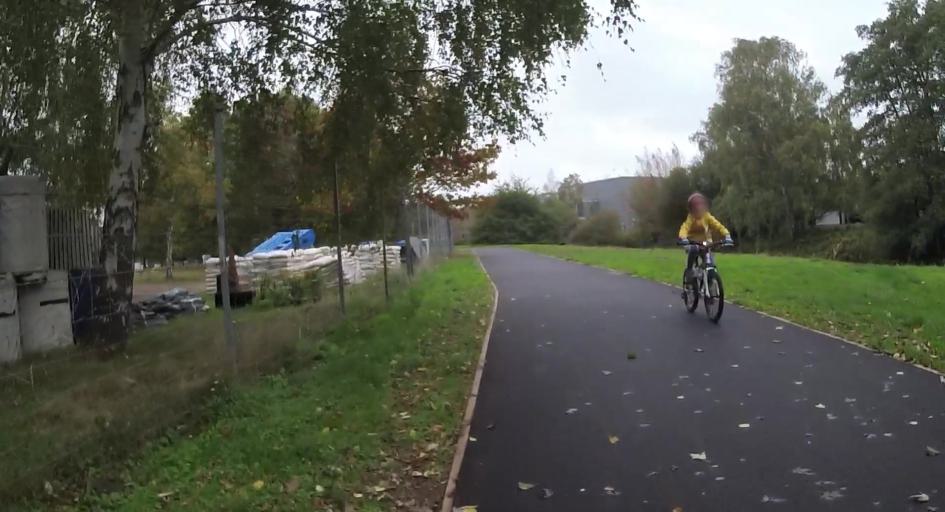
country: GB
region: England
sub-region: Surrey
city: Byfleet
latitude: 51.3487
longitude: -0.4676
